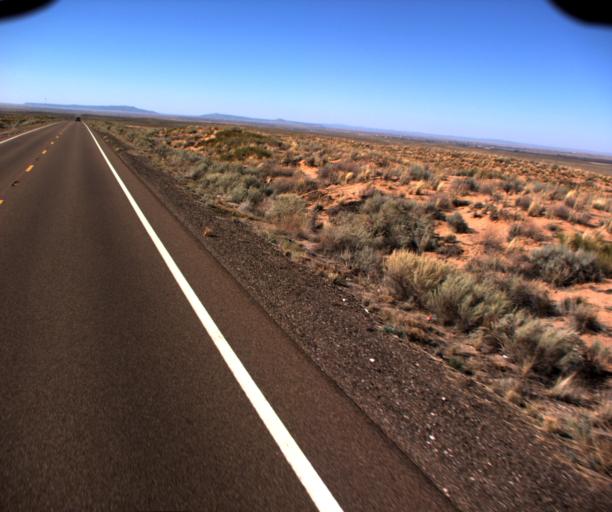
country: US
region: Arizona
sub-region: Navajo County
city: Winslow
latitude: 35.0530
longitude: -110.5941
